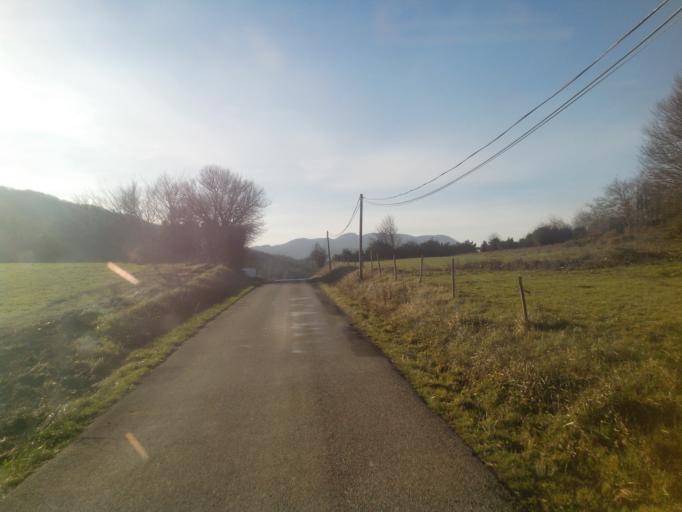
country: FR
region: Languedoc-Roussillon
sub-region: Departement des Pyrenees-Orientales
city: Saint-Paul-de-Fenouillet
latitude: 42.8791
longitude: 2.3864
